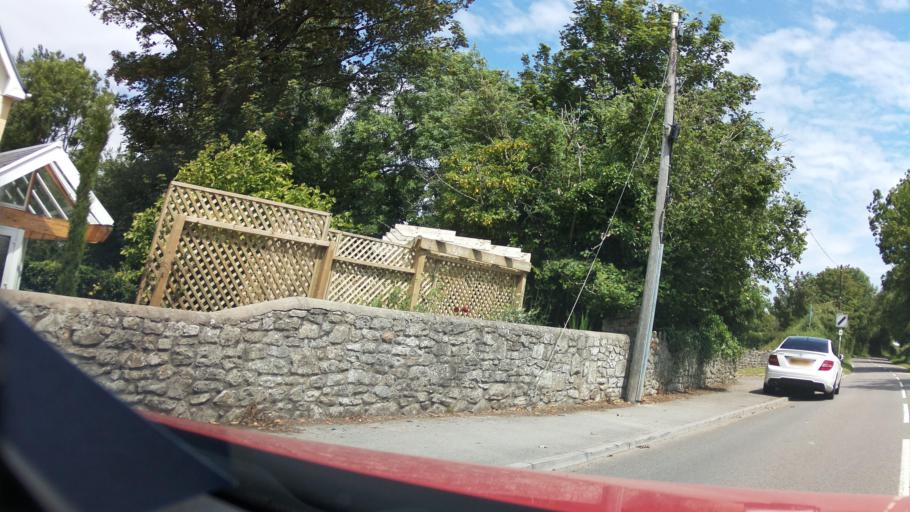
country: GB
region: Wales
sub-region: Bridgend county borough
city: Bridgend
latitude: 51.4850
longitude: -3.5560
